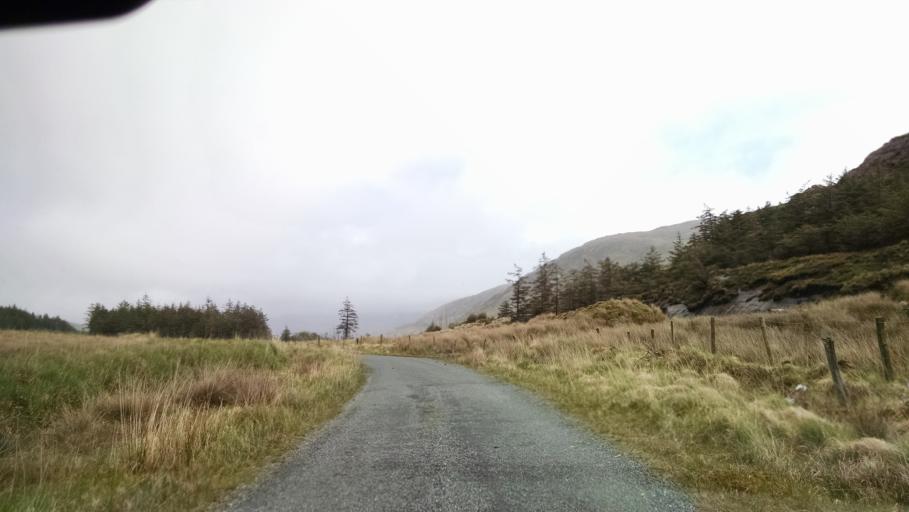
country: IE
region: Connaught
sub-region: Maigh Eo
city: Westport
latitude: 53.6432
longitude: -9.6825
